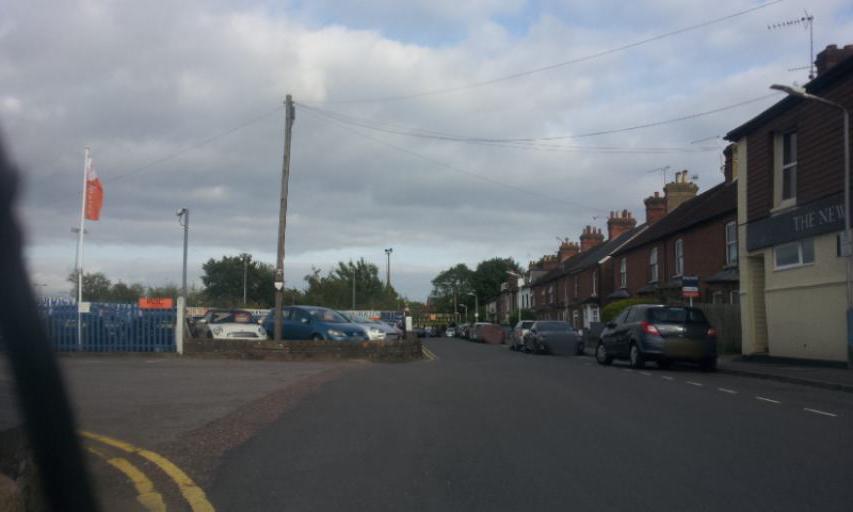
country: GB
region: England
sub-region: Kent
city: Tonbridge
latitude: 51.1905
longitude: 0.2736
